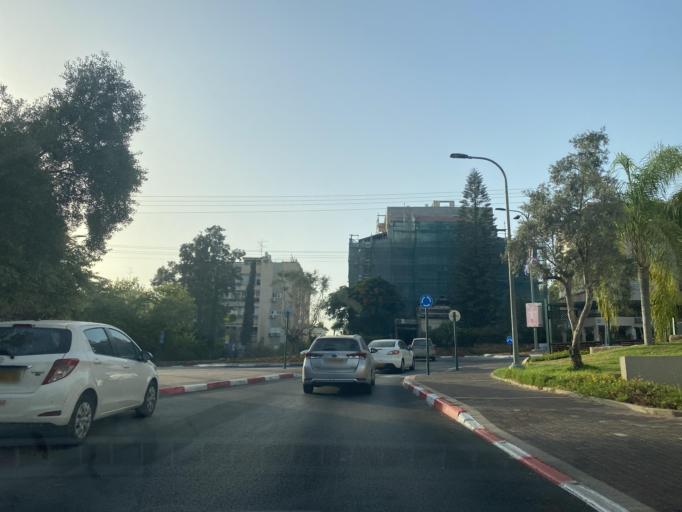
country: IL
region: Central District
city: Hod HaSharon
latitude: 32.1584
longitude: 34.9011
